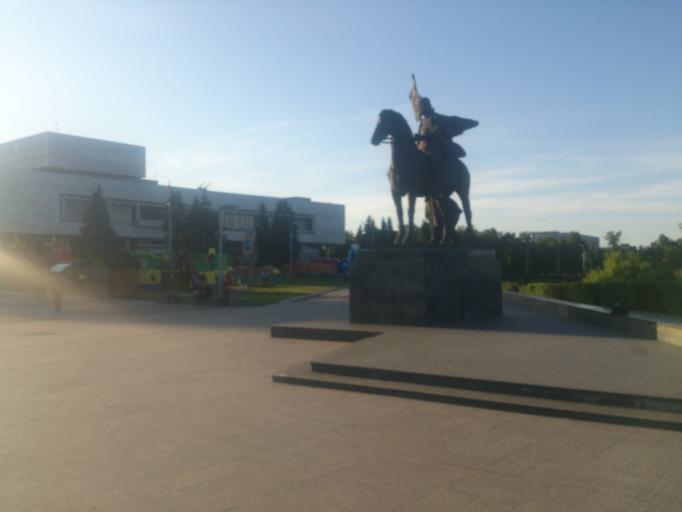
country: RU
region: Ulyanovsk
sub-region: Ulyanovskiy Rayon
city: Ulyanovsk
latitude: 54.3180
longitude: 48.4081
